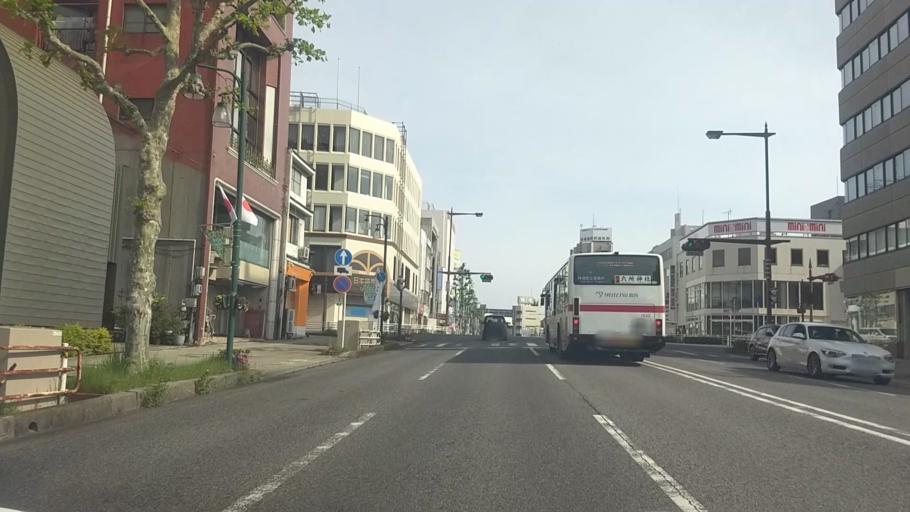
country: JP
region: Aichi
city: Okazaki
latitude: 34.9579
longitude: 137.1639
